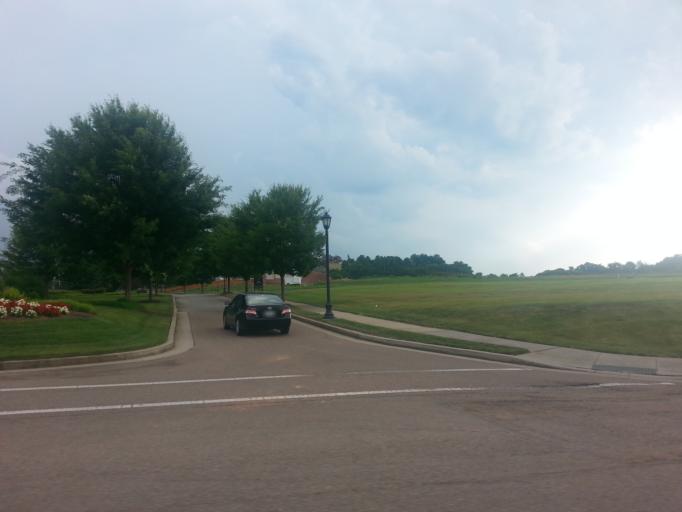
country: US
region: Tennessee
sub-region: Knox County
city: Farragut
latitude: 35.8560
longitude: -84.1960
